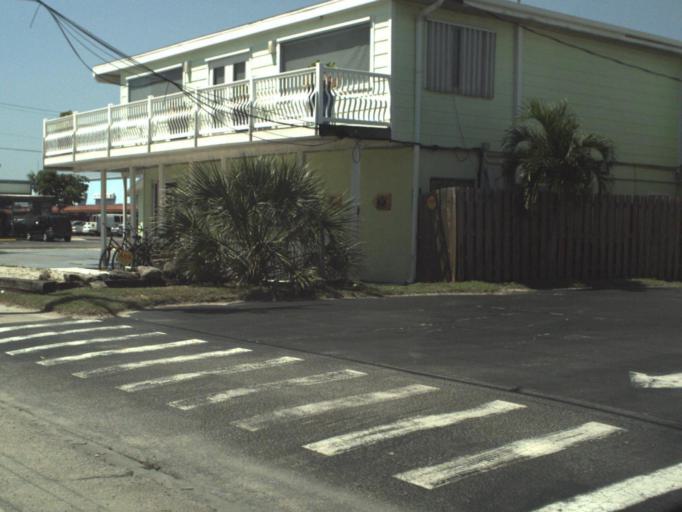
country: US
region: Florida
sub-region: Brevard County
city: Indialantic
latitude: 28.0991
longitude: -80.5693
